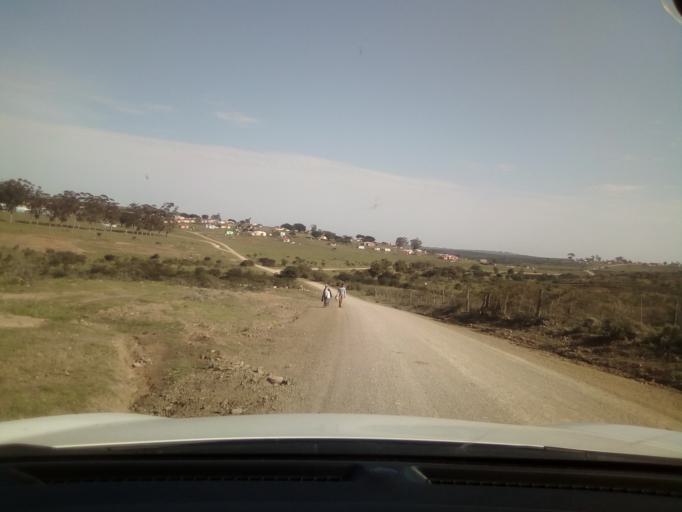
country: ZA
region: Eastern Cape
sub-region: Buffalo City Metropolitan Municipality
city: Bhisho
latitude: -32.9885
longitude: 27.2421
